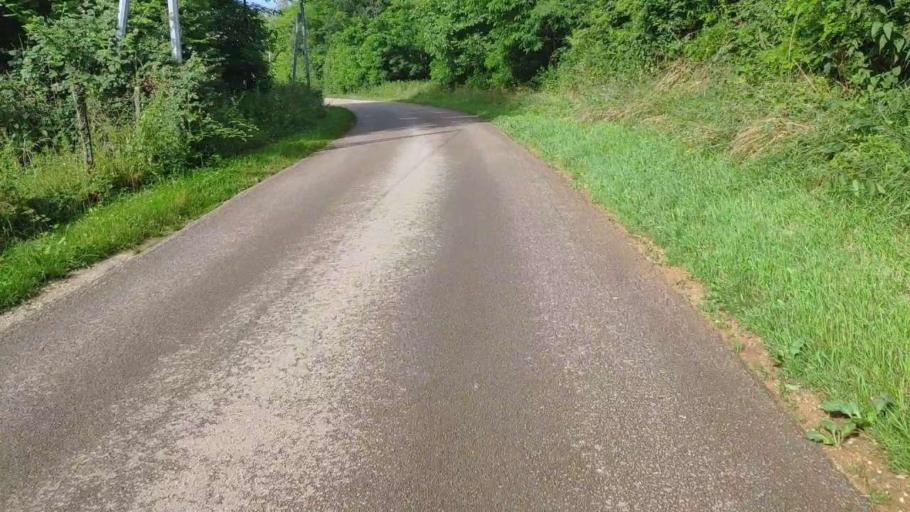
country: FR
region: Franche-Comte
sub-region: Departement du Jura
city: Poligny
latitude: 46.8314
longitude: 5.5765
